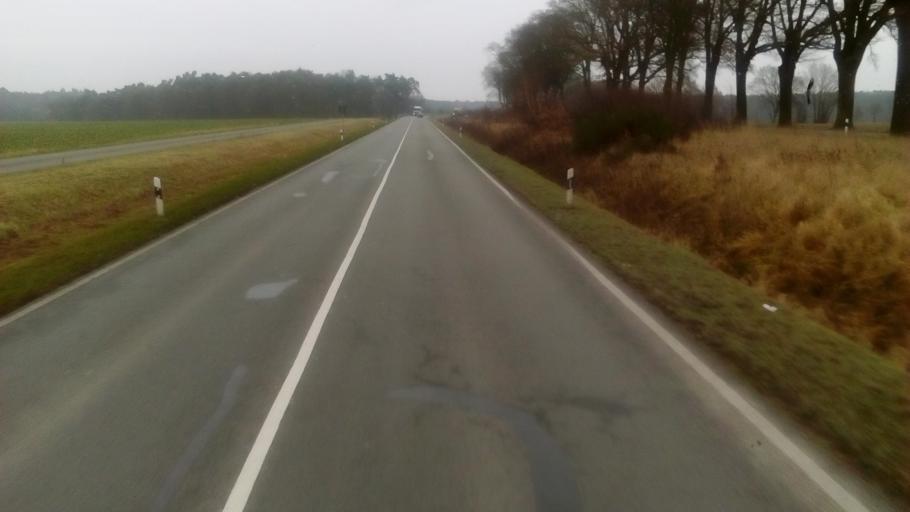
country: DE
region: Brandenburg
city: Gross Pankow
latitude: 53.1275
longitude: 12.0552
